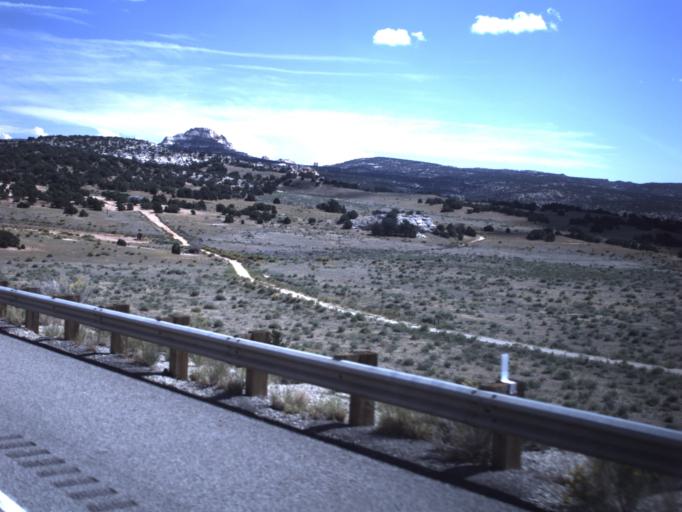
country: US
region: Utah
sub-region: Emery County
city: Ferron
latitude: 38.8472
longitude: -110.8968
